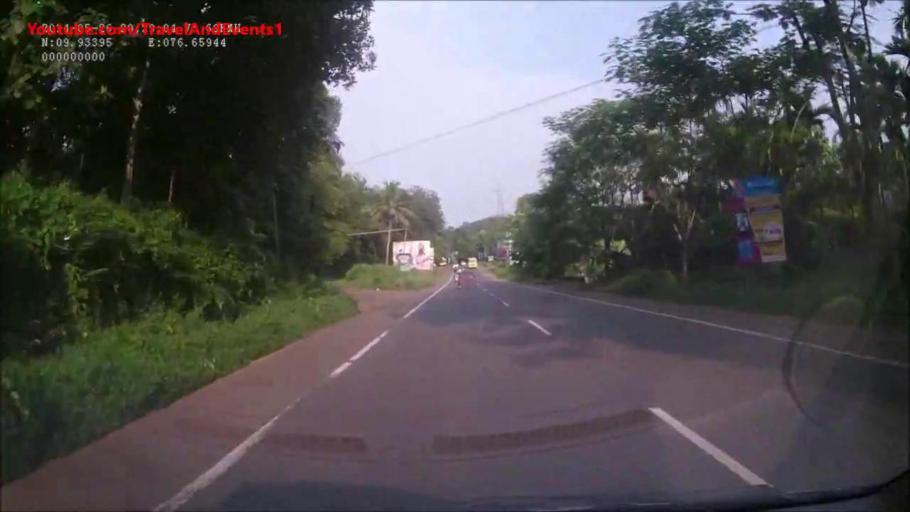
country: IN
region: Kerala
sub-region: Ernakulam
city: Muvattupula
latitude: 9.9314
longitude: 76.6646
